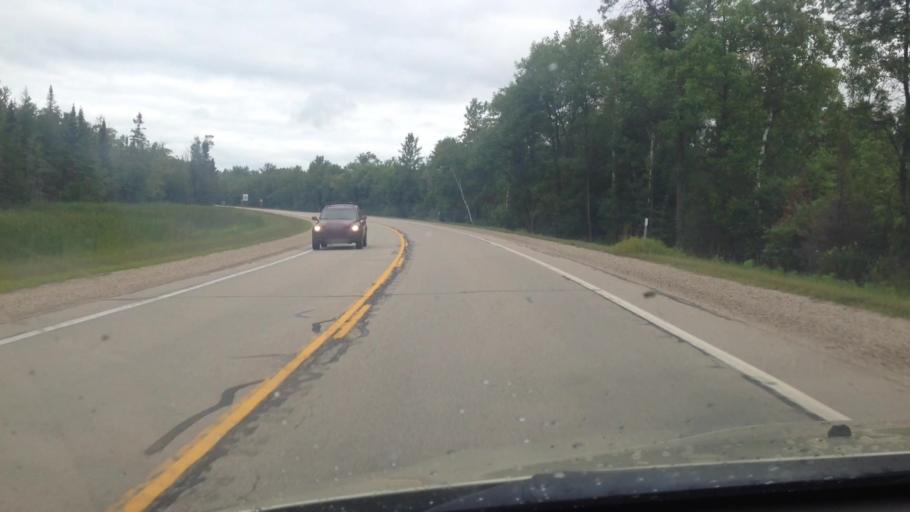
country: US
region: Michigan
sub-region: Menominee County
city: Menominee
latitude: 45.4197
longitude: -87.3466
